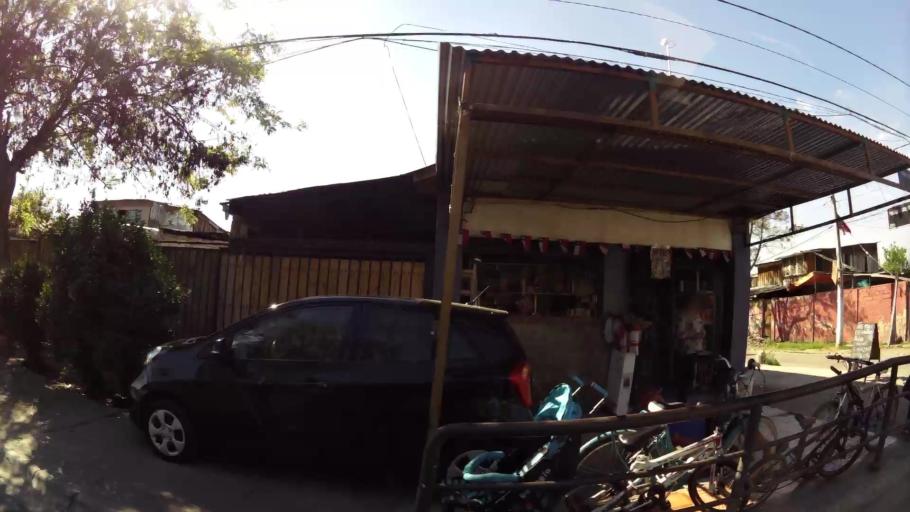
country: CL
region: Santiago Metropolitan
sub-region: Provincia de Santiago
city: La Pintana
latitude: -33.5388
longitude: -70.6173
